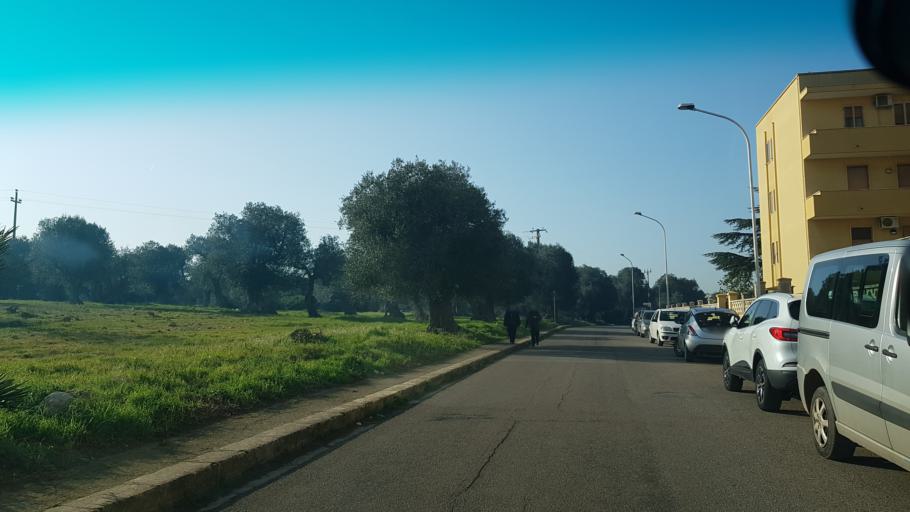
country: IT
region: Apulia
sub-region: Provincia di Brindisi
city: San Vito dei Normanni
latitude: 40.6635
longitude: 17.6944
